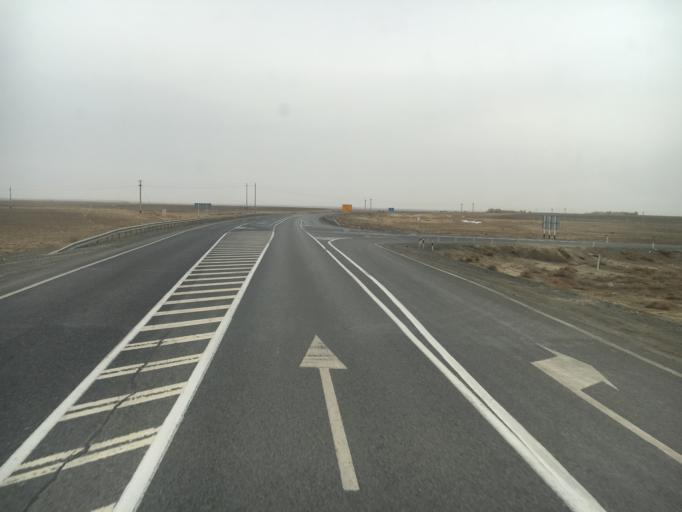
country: KZ
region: Qyzylorda
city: Aral
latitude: 46.8232
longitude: 61.7064
